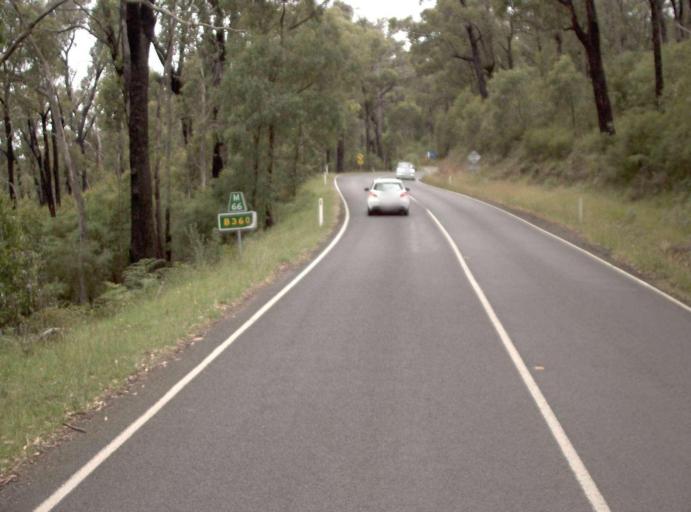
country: AU
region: Victoria
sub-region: Yarra Ranges
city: Healesville
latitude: -37.6471
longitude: 145.5667
